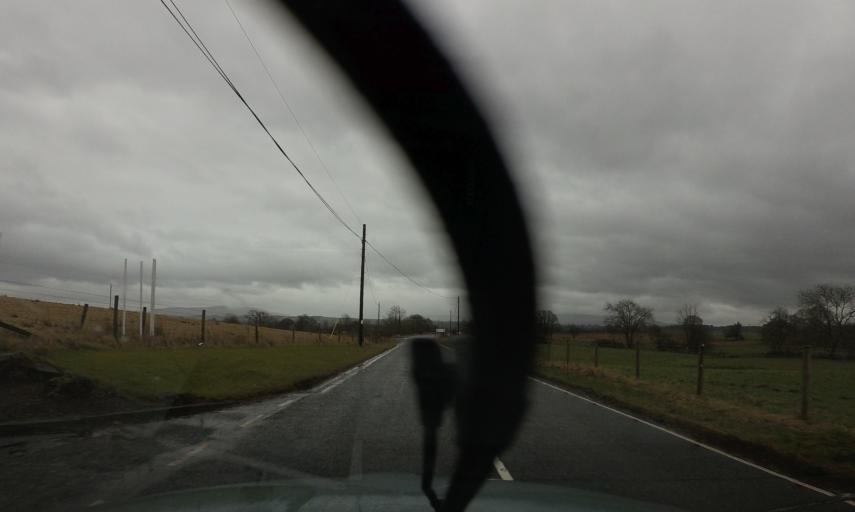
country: GB
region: Scotland
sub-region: Stirling
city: Balfron
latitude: 56.1386
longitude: -4.3602
